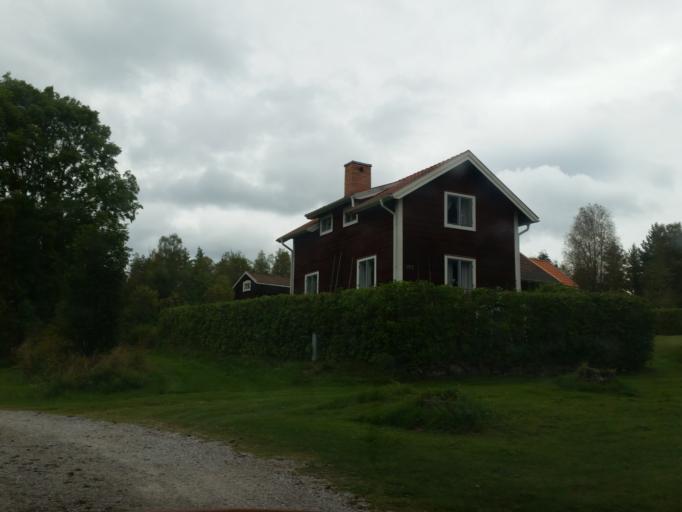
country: SE
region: Dalarna
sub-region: Leksand Municipality
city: Smedby
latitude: 60.6807
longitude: 15.1718
